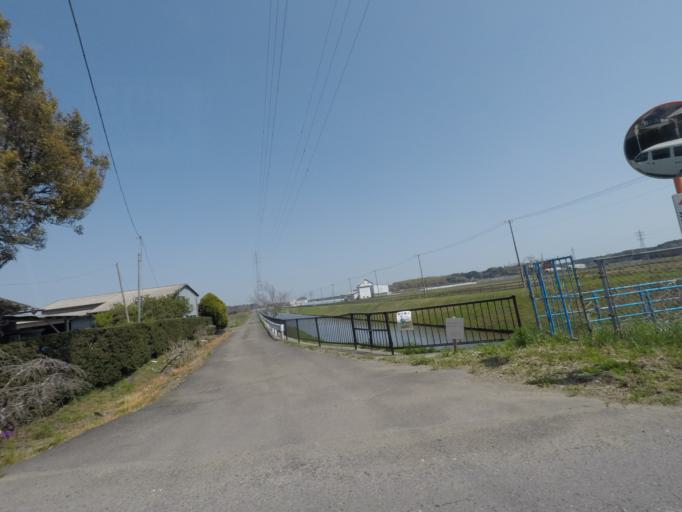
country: JP
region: Chiba
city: Yokaichiba
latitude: 35.6783
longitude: 140.4661
